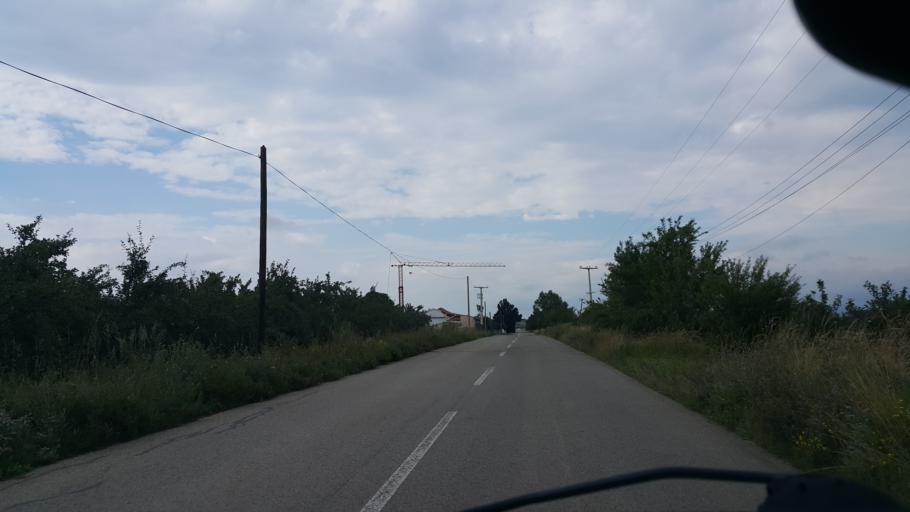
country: RS
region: Central Serbia
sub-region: Toplicki Okrug
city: Blace
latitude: 43.2350
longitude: 21.2564
